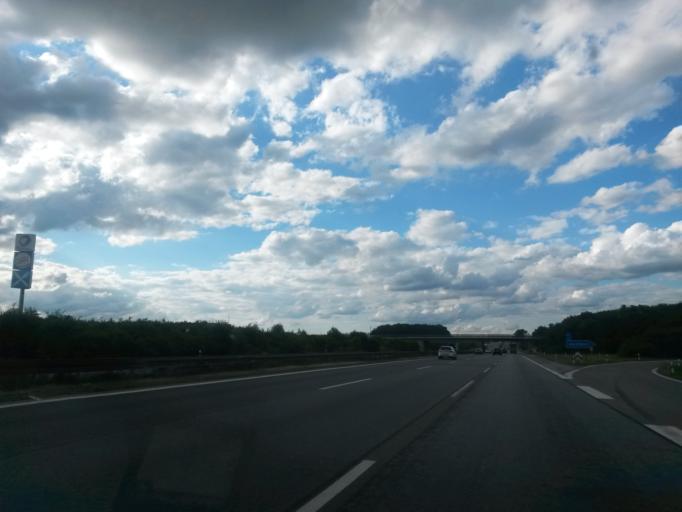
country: DE
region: Bavaria
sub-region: Upper Palatinate
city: Freystadt
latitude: 49.1598
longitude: 11.2645
